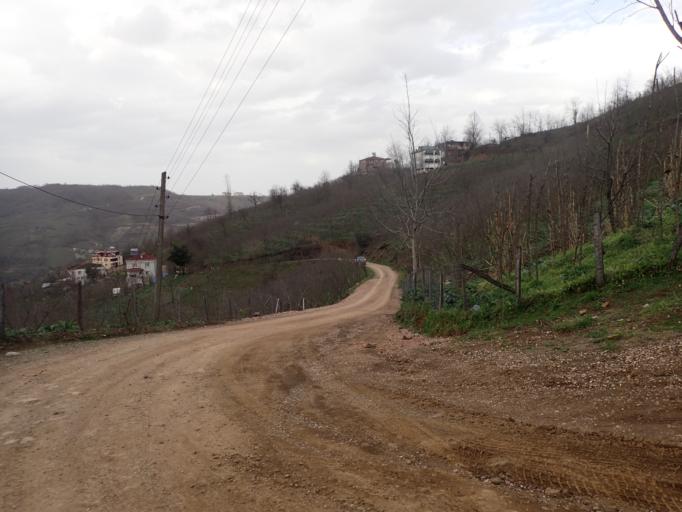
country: TR
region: Ordu
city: Camas
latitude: 40.8887
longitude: 37.4969
